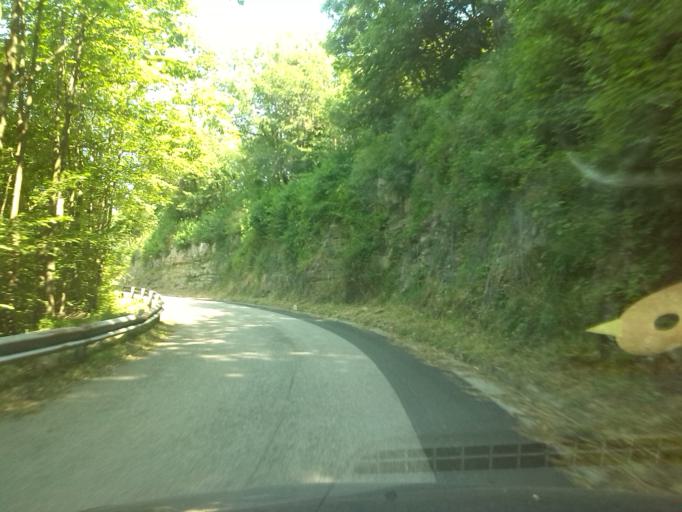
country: IT
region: Friuli Venezia Giulia
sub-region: Provincia di Udine
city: Clodig
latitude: 46.1319
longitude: 13.6119
